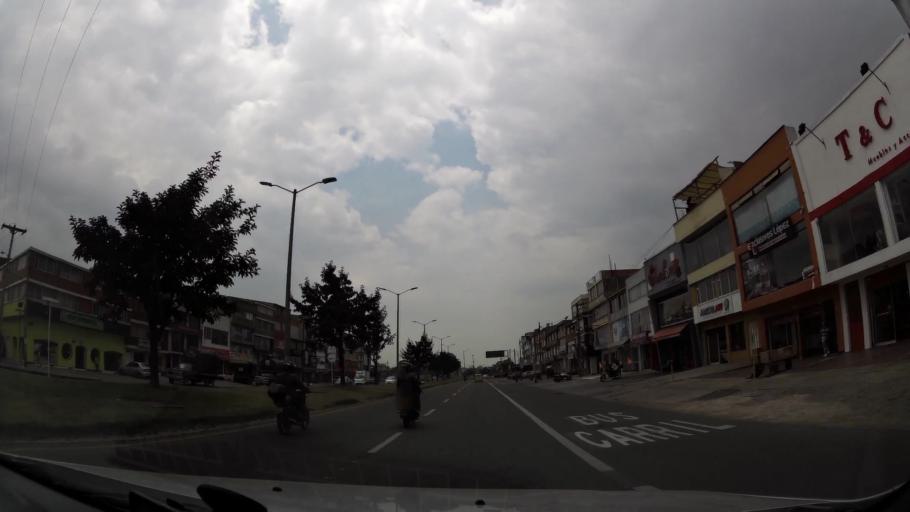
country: CO
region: Bogota D.C.
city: Bogota
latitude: 4.6014
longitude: -74.1193
